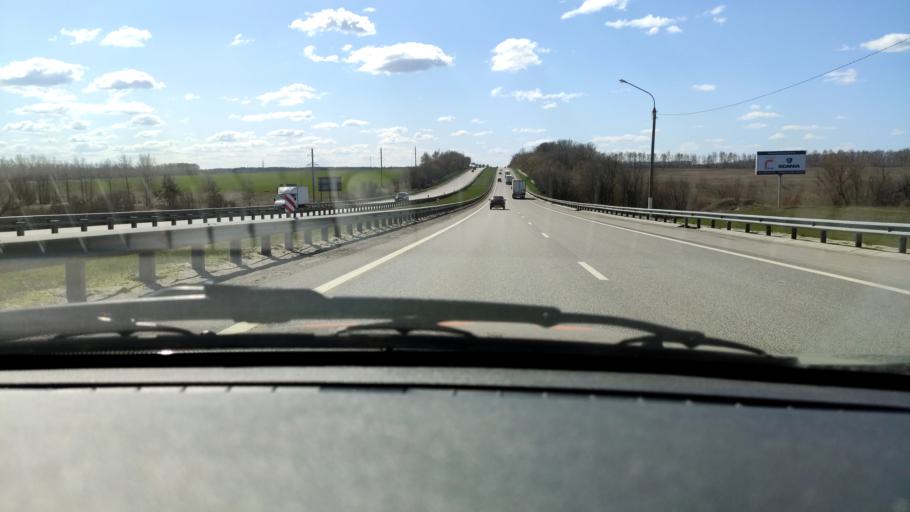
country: RU
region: Voronezj
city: Ramon'
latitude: 51.9200
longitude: 39.2192
